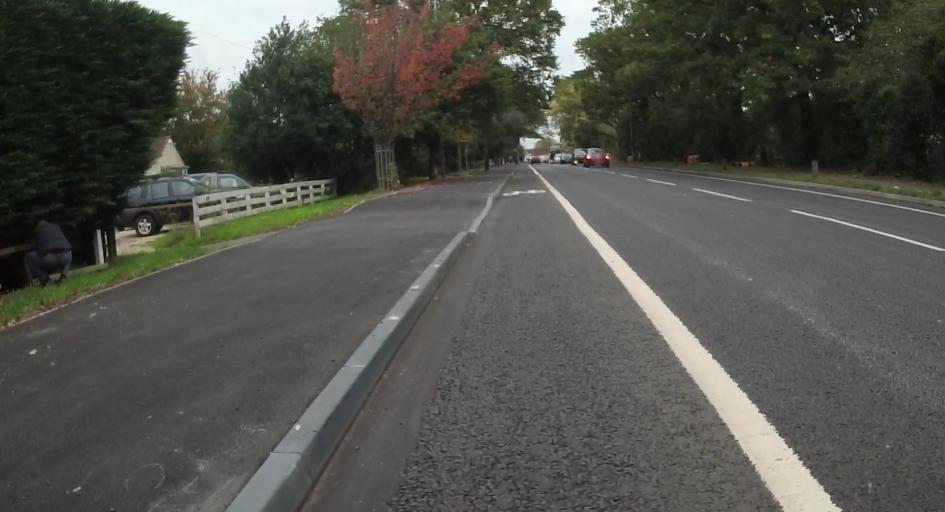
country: GB
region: England
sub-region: Wokingham
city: Wokingham
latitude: 51.4113
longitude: -0.8103
